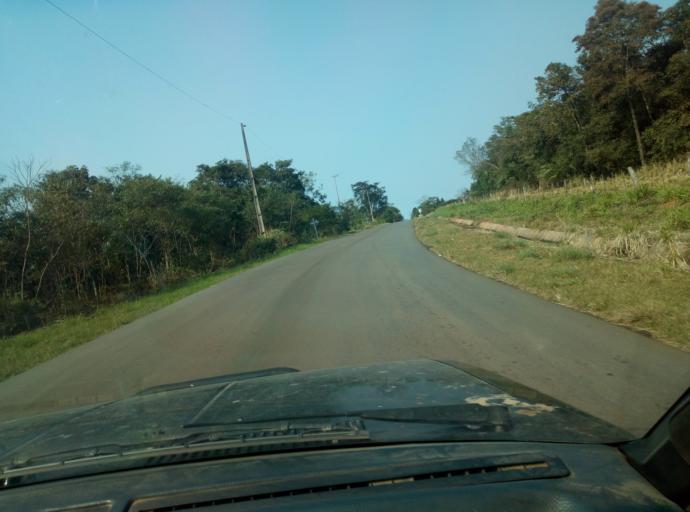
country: PY
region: Caaguazu
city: Carayao
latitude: -25.2064
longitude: -56.3064
